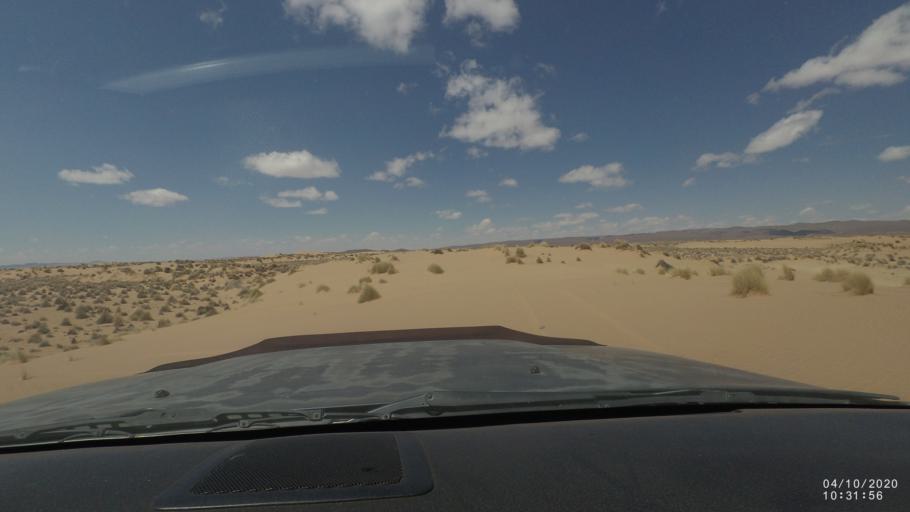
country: BO
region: Oruro
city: Poopo
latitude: -18.7044
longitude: -67.4830
